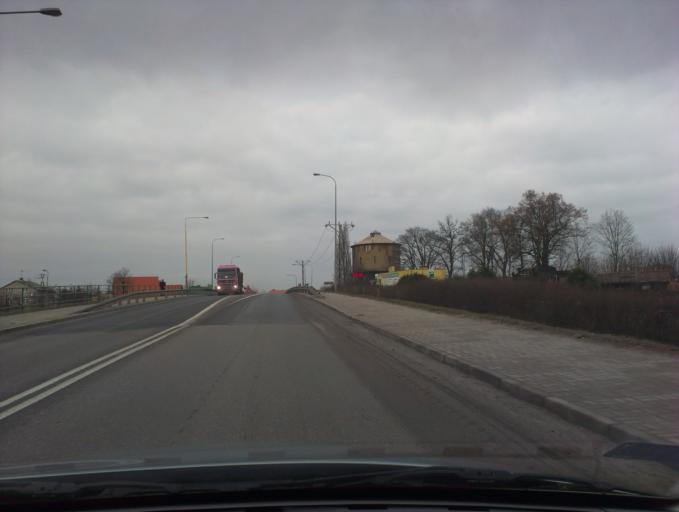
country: PL
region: West Pomeranian Voivodeship
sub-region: Powiat szczecinecki
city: Szczecinek
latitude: 53.6904
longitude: 16.7022
